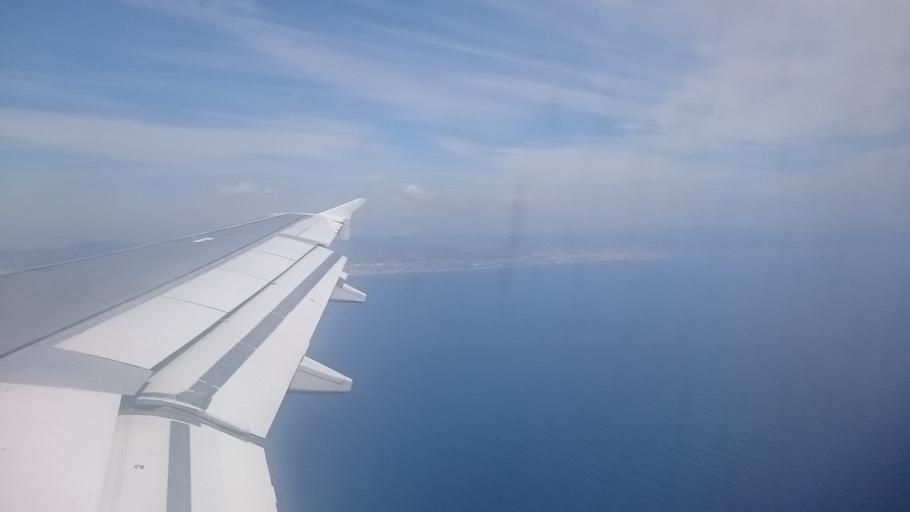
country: ES
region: Catalonia
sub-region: Provincia de Barcelona
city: Premia de Mar
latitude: 41.4104
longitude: 2.4109
